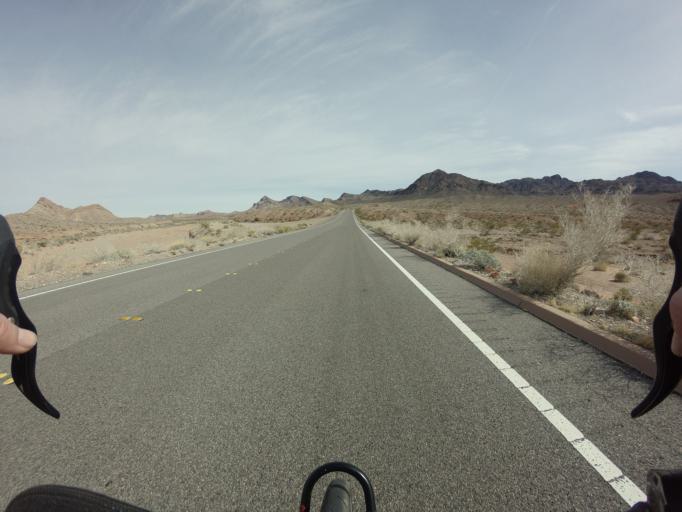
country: US
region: Nevada
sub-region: Clark County
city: Boulder City
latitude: 36.1962
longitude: -114.6890
